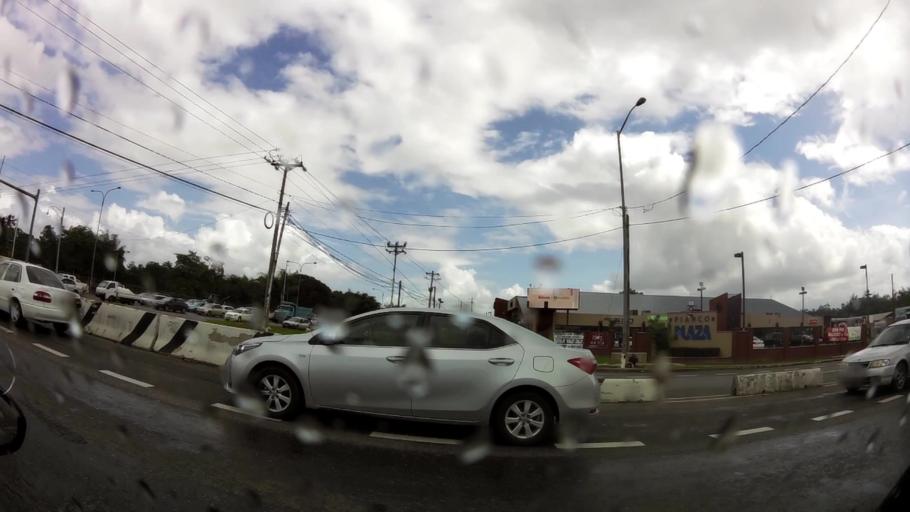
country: TT
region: Tunapuna/Piarco
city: Arouca
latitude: 10.6153
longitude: -61.3438
